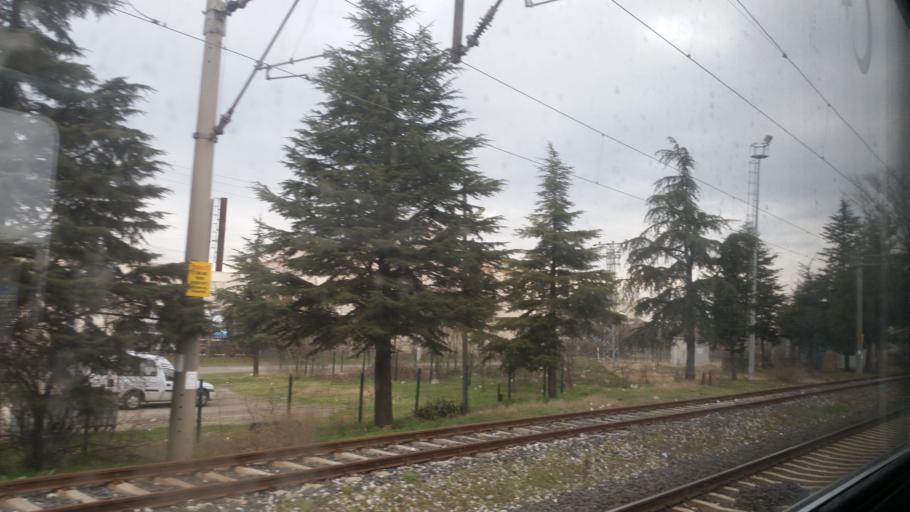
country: TR
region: Tekirdag
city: Velimese
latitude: 41.2452
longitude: 27.8847
